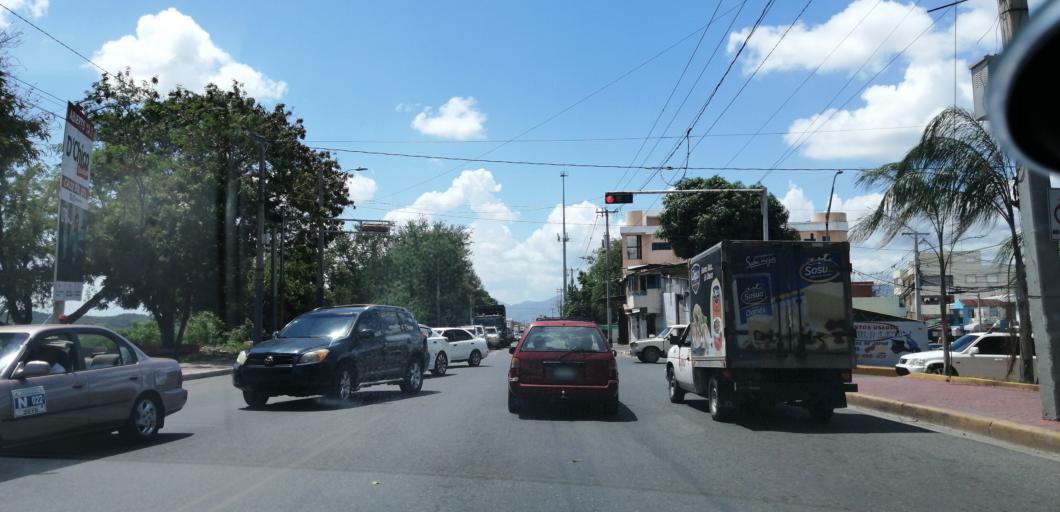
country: DO
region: Santiago
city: Santiago de los Caballeros
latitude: 19.4348
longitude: -70.6967
